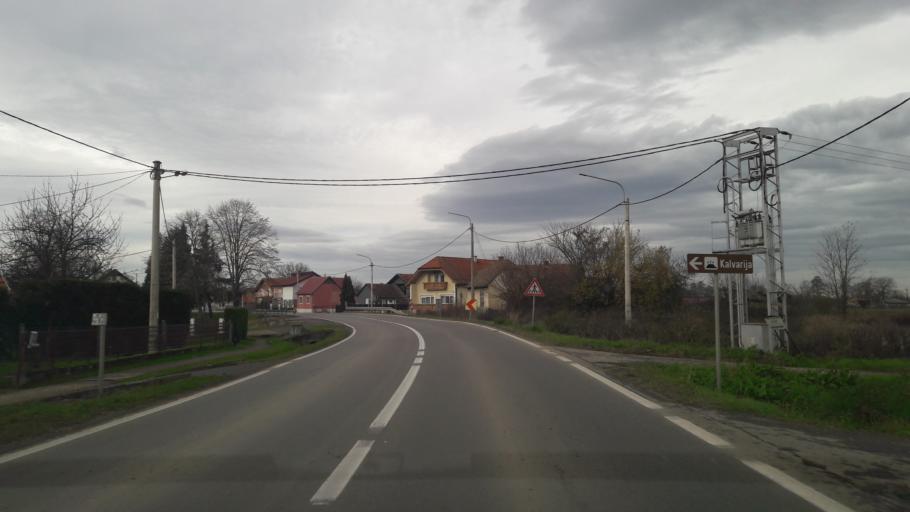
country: HR
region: Osjecko-Baranjska
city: Fericanci
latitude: 45.5232
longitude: 17.9958
